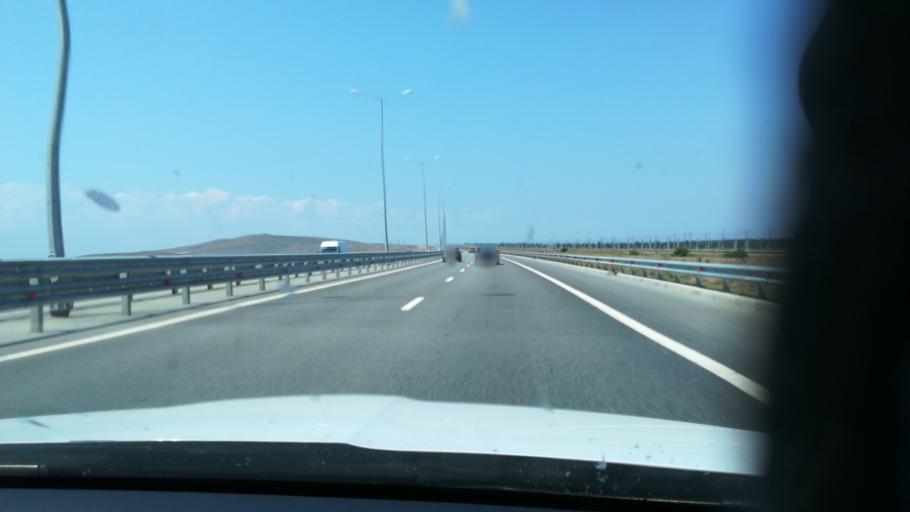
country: RU
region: Krasnodarskiy
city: Vyshestebliyevskaya
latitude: 45.2295
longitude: 36.9316
